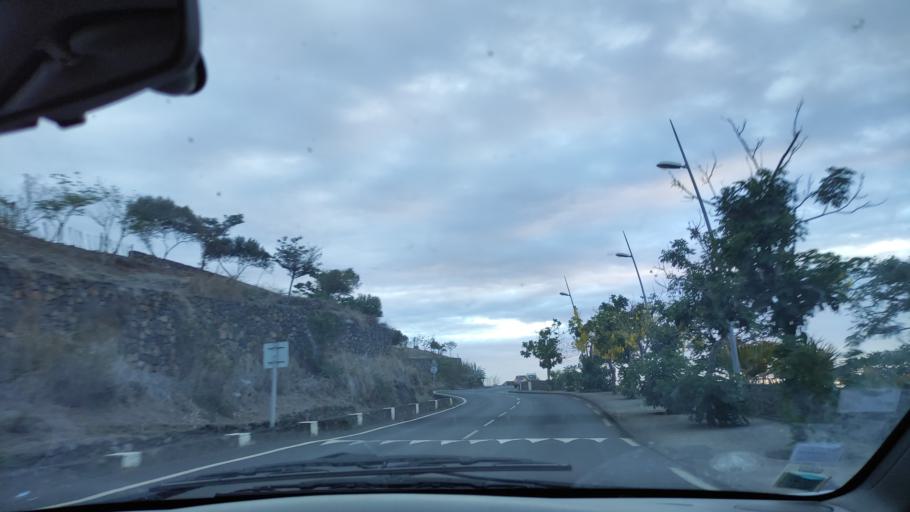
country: RE
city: Piton Saint-Leu
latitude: -21.2028
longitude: 55.2942
